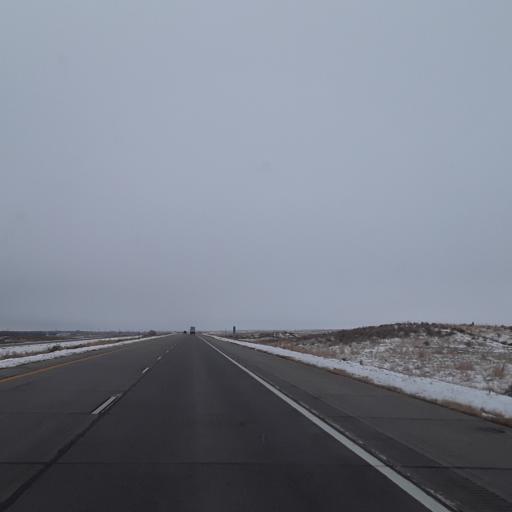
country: US
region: Colorado
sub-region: Logan County
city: Sterling
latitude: 40.5577
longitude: -103.2128
